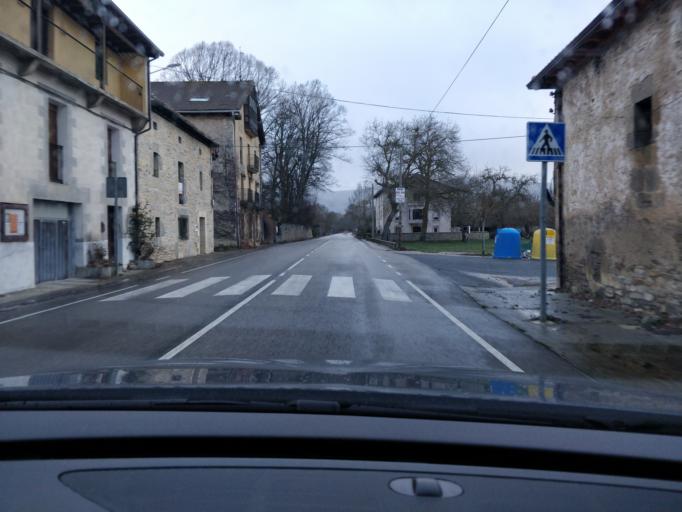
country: ES
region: Castille and Leon
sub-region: Provincia de Burgos
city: Espinosa de los Monteros
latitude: 43.0612
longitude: -3.4956
